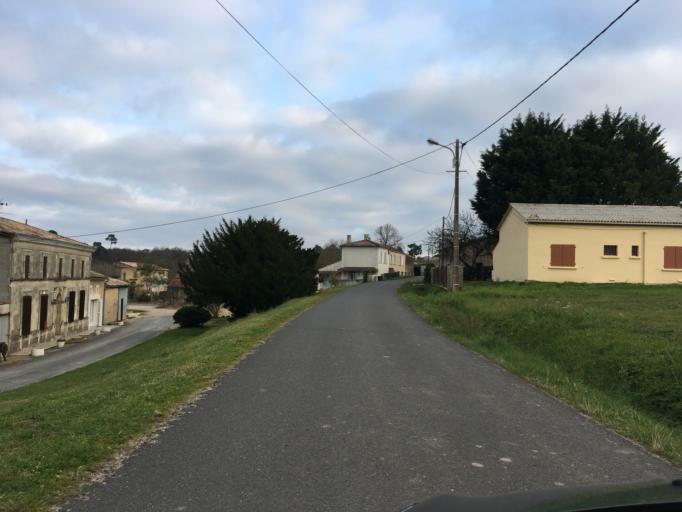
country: FR
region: Aquitaine
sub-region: Departement de la Gironde
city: Saint-Ciers-sur-Gironde
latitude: 45.3144
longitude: -0.6141
